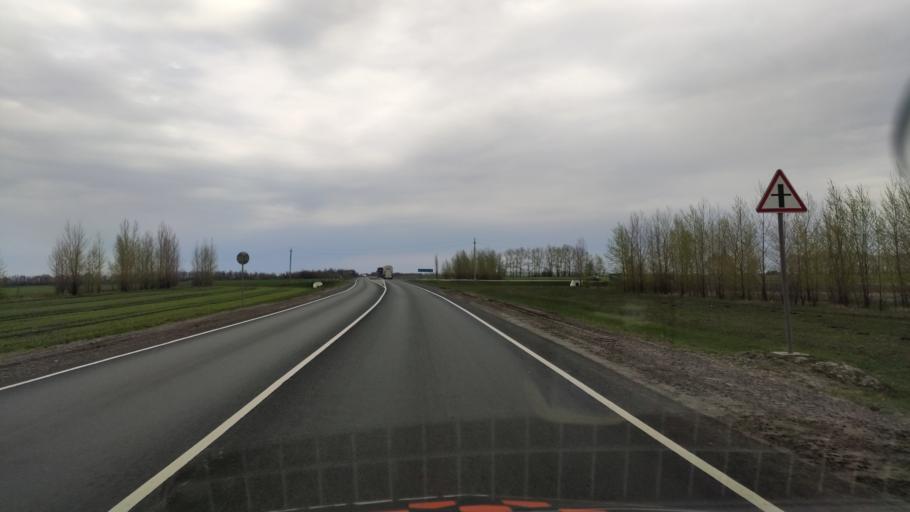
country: RU
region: Voronezj
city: Nizhnedevitsk
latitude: 51.5999
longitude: 38.6011
